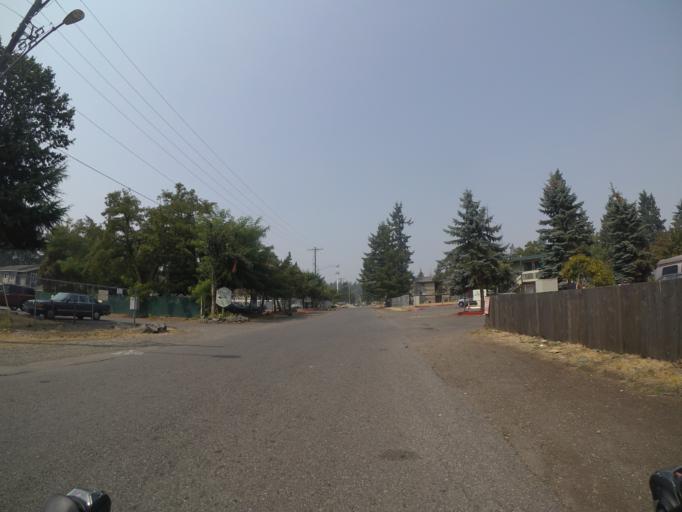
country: US
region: Washington
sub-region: Pierce County
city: McChord Air Force Base
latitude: 47.1413
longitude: -122.5111
